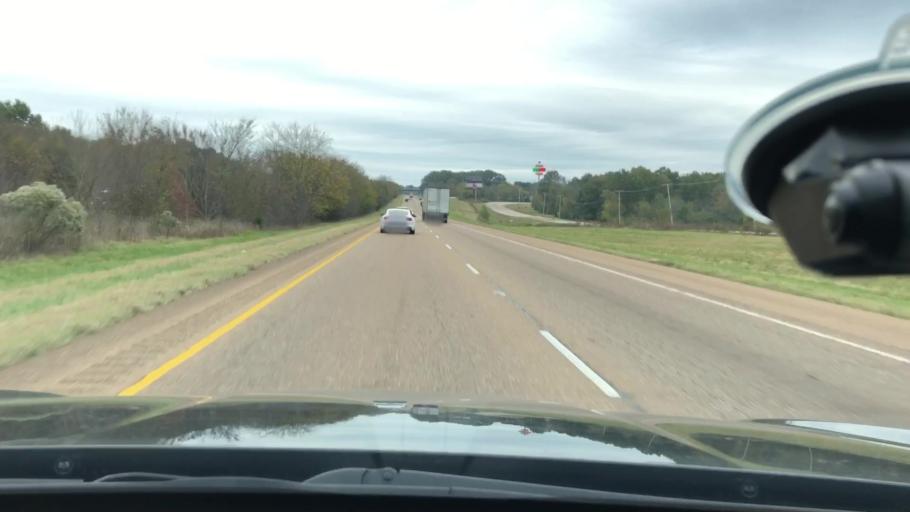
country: US
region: Arkansas
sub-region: Nevada County
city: Prescott
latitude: 33.8252
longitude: -93.4033
